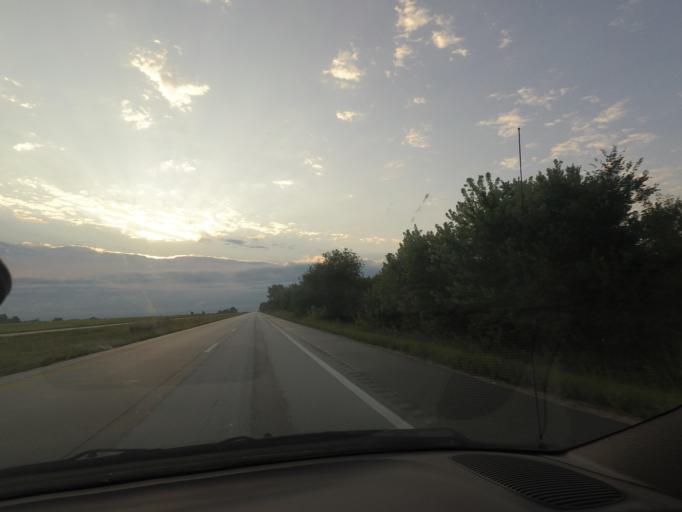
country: US
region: Missouri
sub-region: Shelby County
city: Shelbina
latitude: 39.7300
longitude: -92.1958
